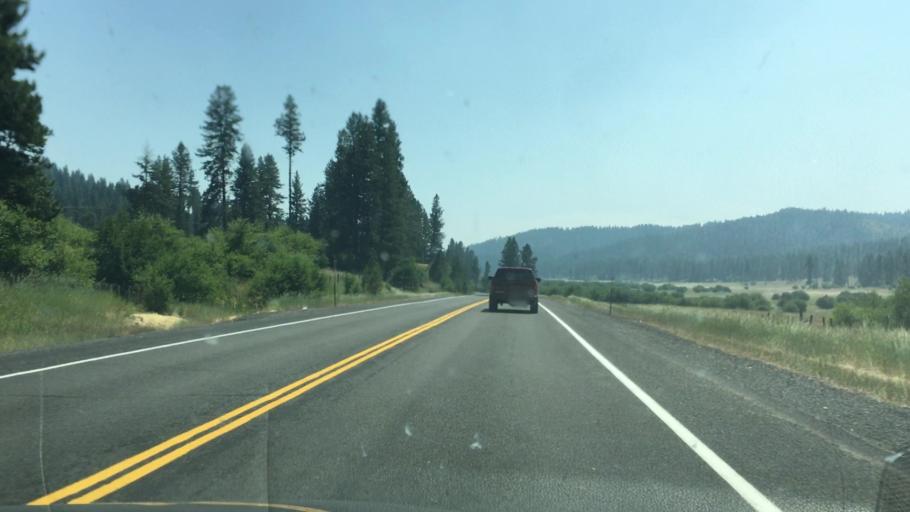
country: US
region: Idaho
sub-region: Valley County
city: McCall
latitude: 45.0903
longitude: -116.3066
